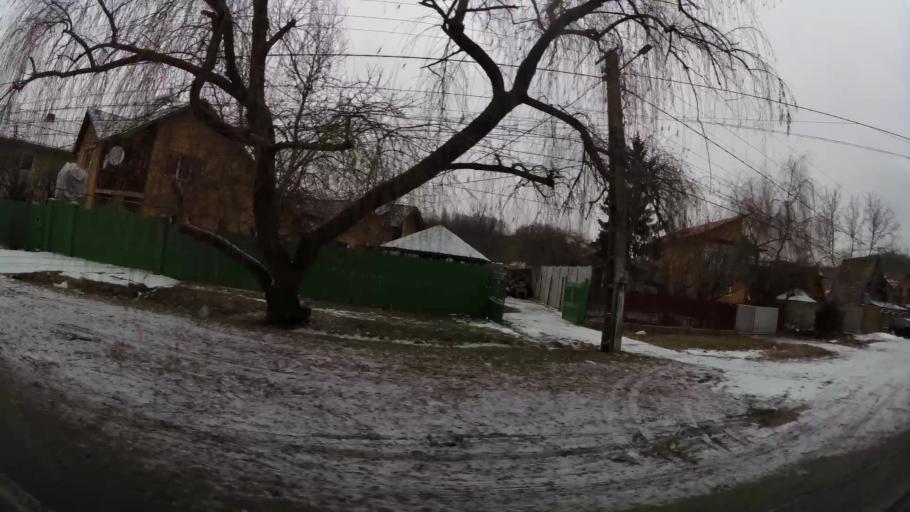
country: RO
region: Dambovita
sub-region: Comuna Aninoasa
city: Viforata
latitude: 44.9442
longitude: 25.4872
